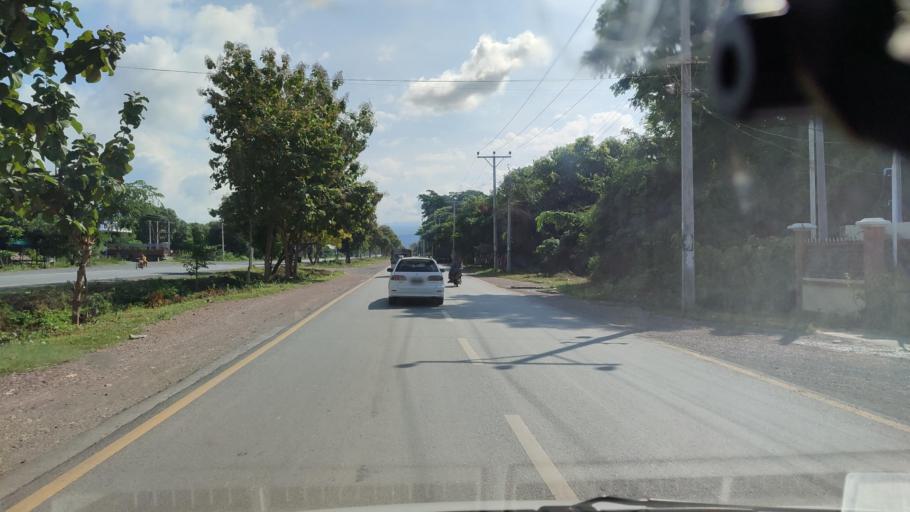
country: MM
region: Mandalay
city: Mandalay
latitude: 21.8778
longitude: 96.2049
